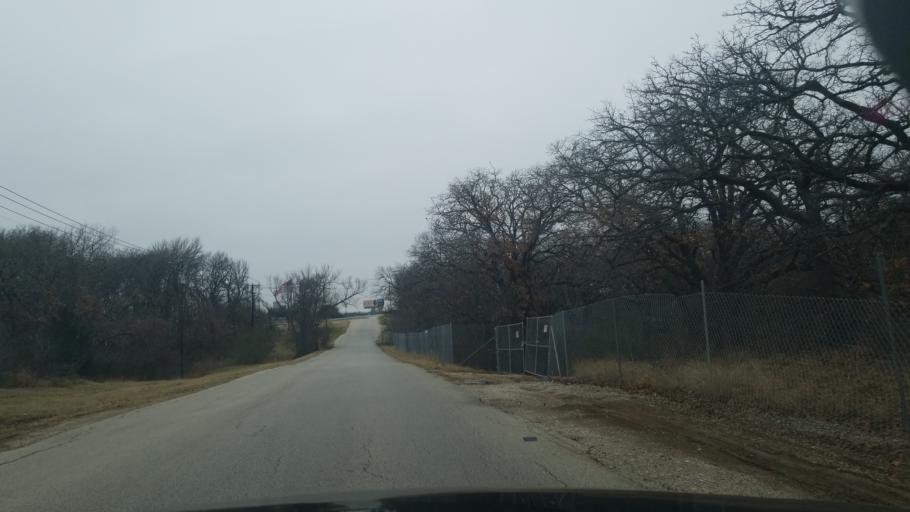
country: US
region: Texas
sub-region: Denton County
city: Corinth
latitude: 33.1643
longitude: -97.0744
